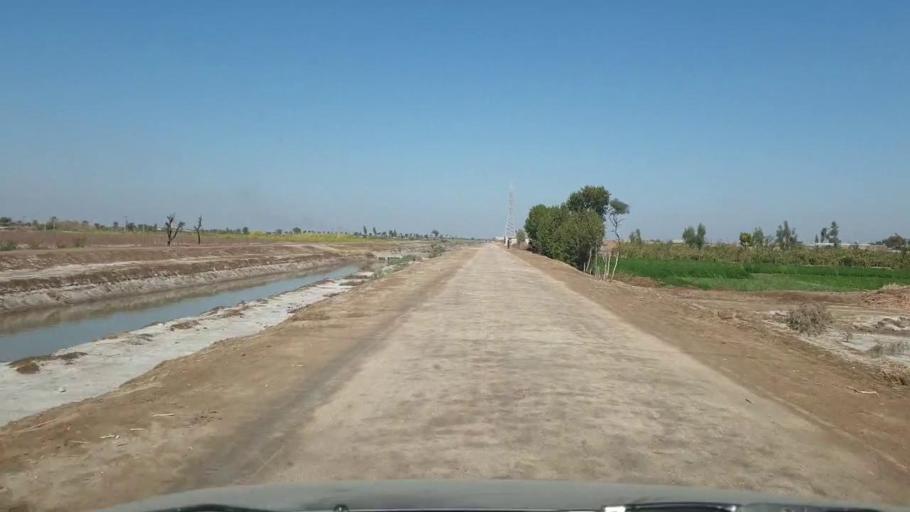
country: PK
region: Sindh
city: Mirwah Gorchani
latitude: 25.3104
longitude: 69.1263
